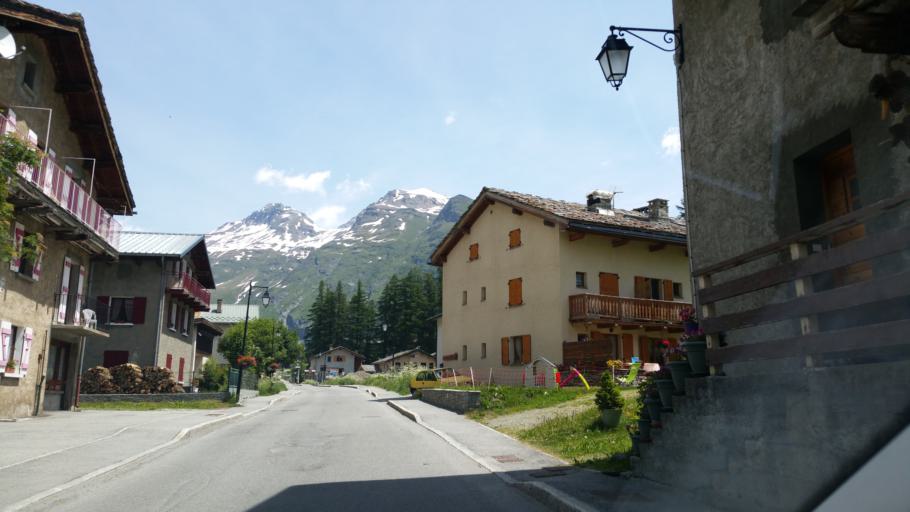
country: IT
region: Piedmont
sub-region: Provincia di Torino
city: Moncenisio
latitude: 45.3222
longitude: 6.9971
